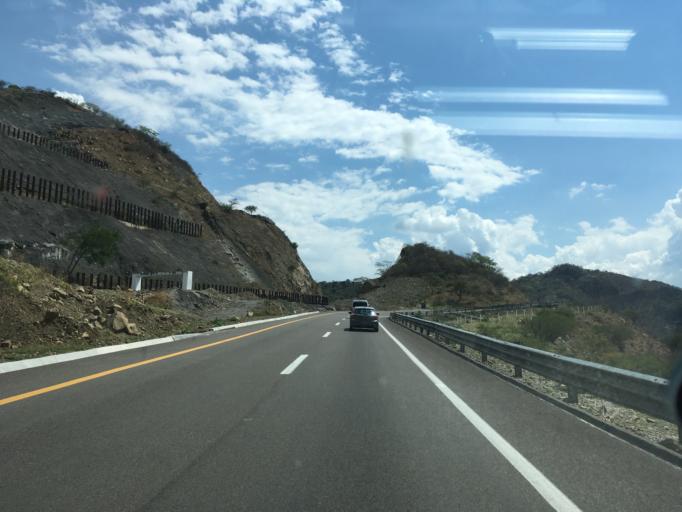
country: MX
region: Puebla
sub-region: San Jose Miahuatlan
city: San Pedro Tetitlan
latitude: 18.1126
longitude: -97.3405
